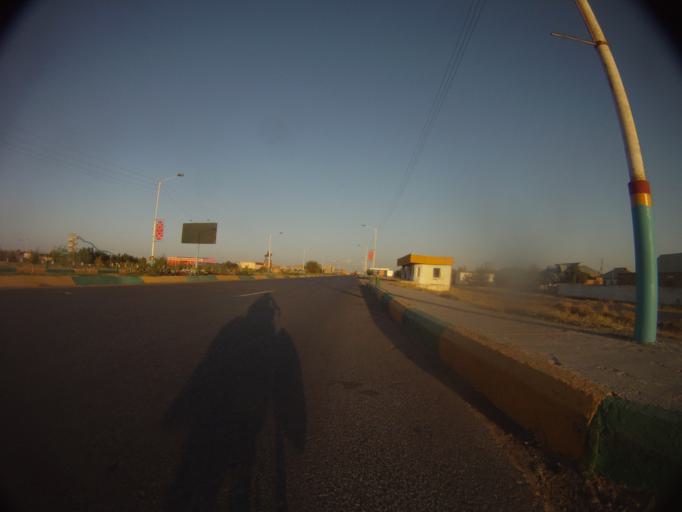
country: KZ
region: Ongtustik Qazaqstan
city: Turkestan
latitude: 43.2854
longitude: 68.3064
